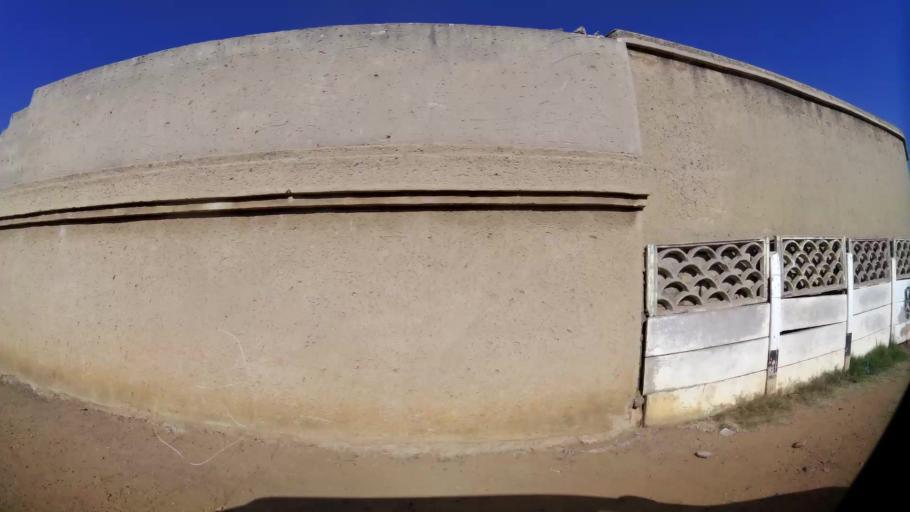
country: ZA
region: Gauteng
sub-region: City of Johannesburg Metropolitan Municipality
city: Soweto
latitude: -26.2504
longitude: 27.9514
